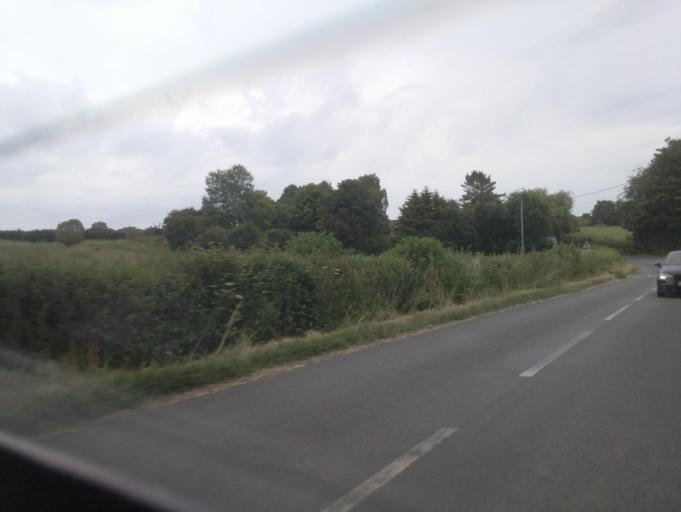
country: GB
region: England
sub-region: Dorset
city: Sherborne
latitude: 50.9219
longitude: -2.5521
